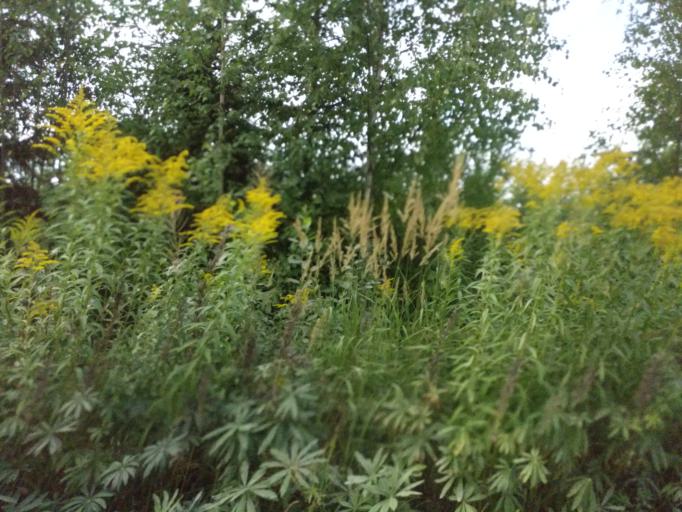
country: SE
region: Vaermland
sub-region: Hagfors Kommun
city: Hagfors
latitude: 60.0156
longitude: 13.6940
